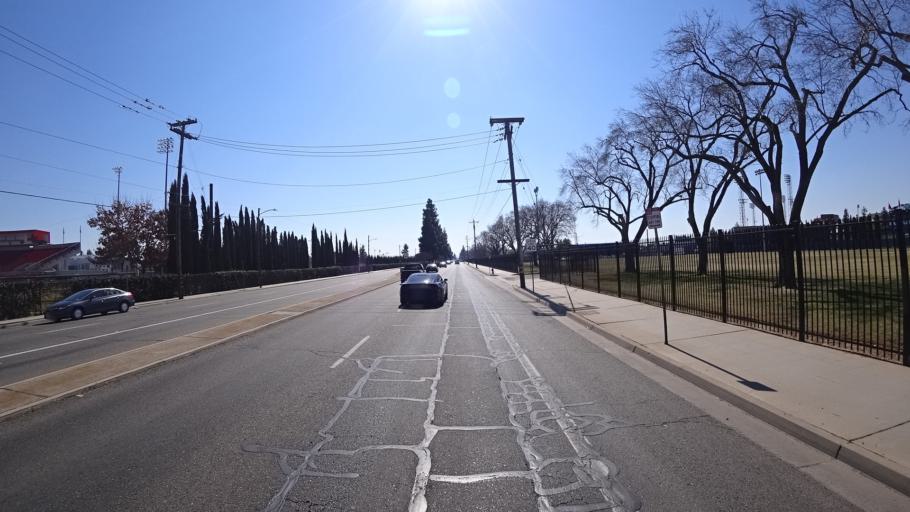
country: US
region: California
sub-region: Fresno County
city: Clovis
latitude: 36.8153
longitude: -119.7543
